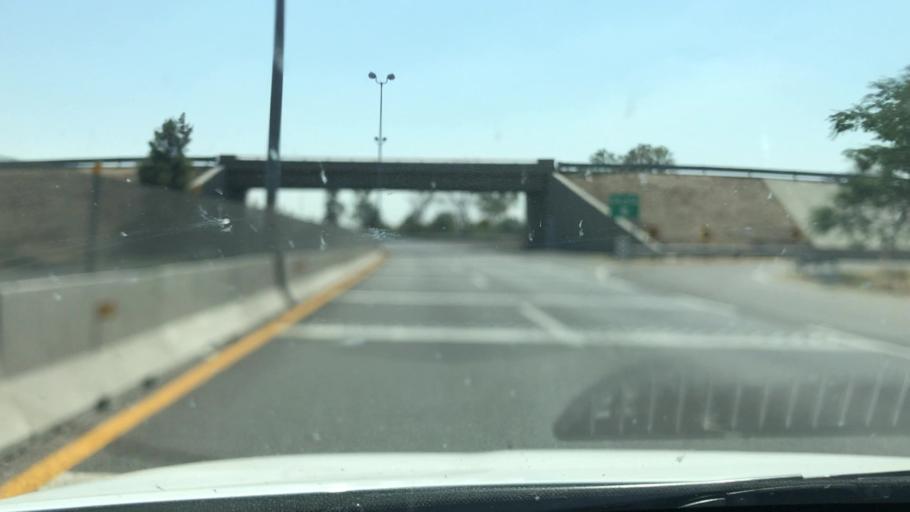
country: MX
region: Guanajuato
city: Abasolo
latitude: 20.4657
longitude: -101.5099
